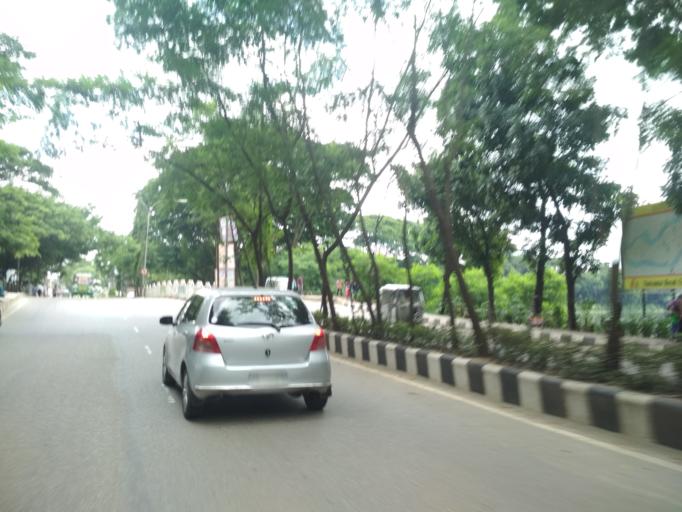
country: BD
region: Dhaka
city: Paltan
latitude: 23.7961
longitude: 90.4184
